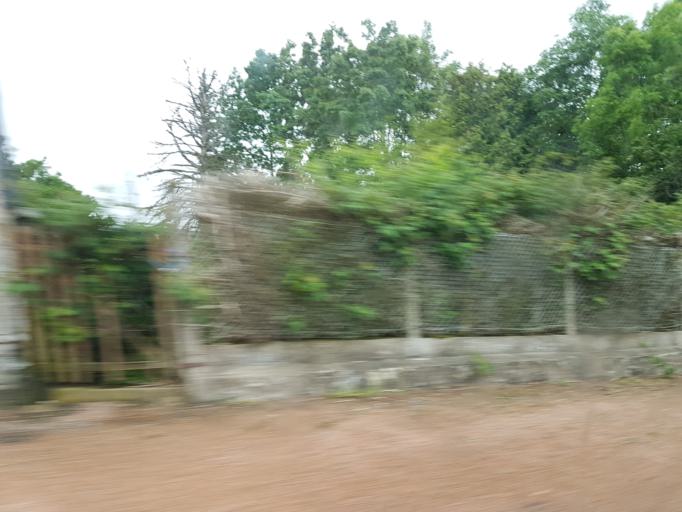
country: FR
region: Bourgogne
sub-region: Departement de la Nievre
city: Chateau-Chinon(Ville)
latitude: 47.0427
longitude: 4.0164
